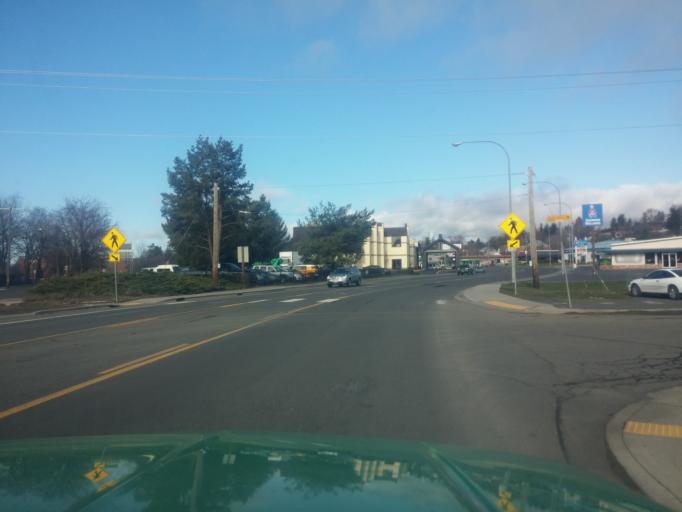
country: US
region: Idaho
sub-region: Latah County
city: Moscow
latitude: 46.7325
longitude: -117.0078
